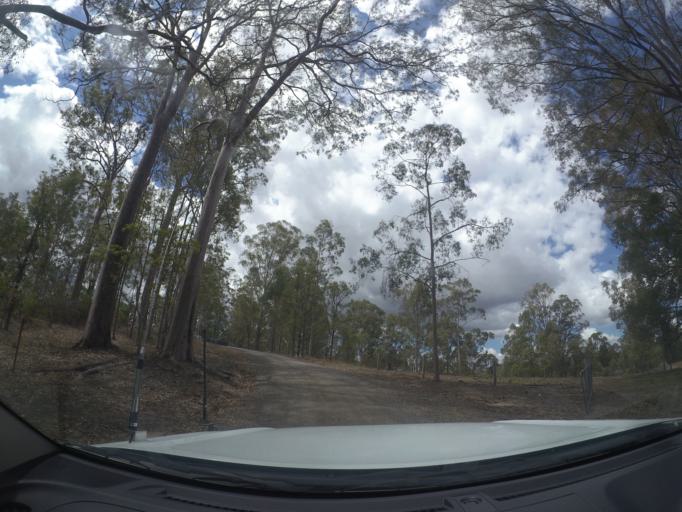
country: AU
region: Queensland
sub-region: Logan
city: Cedar Vale
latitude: -27.9171
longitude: 153.0360
